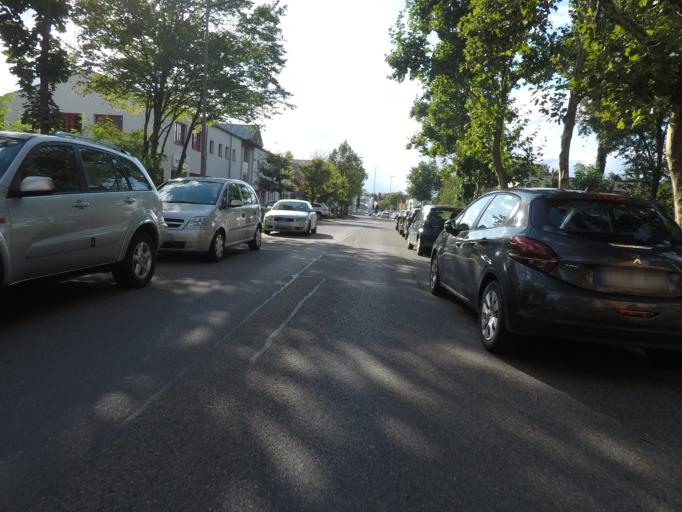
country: DE
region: Baden-Wuerttemberg
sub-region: Tuebingen Region
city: Pfullingen
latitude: 48.4785
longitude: 9.2306
